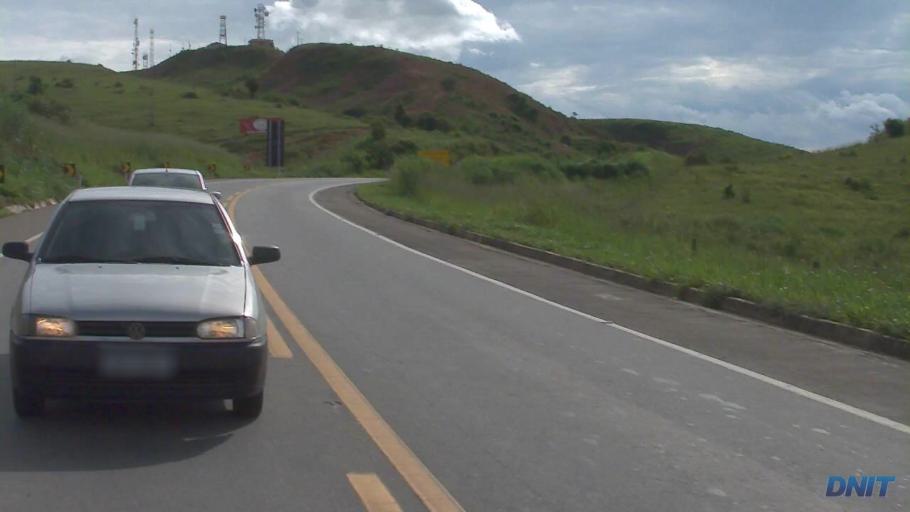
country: BR
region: Minas Gerais
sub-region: Belo Oriente
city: Belo Oriente
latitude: -19.2214
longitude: -42.3216
